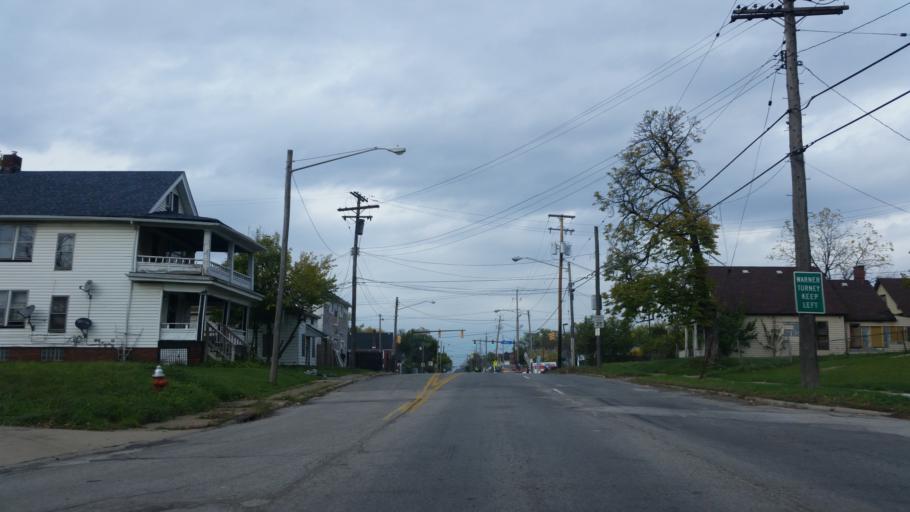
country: US
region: Ohio
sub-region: Cuyahoga County
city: Garfield Heights
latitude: 41.4441
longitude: -81.6214
